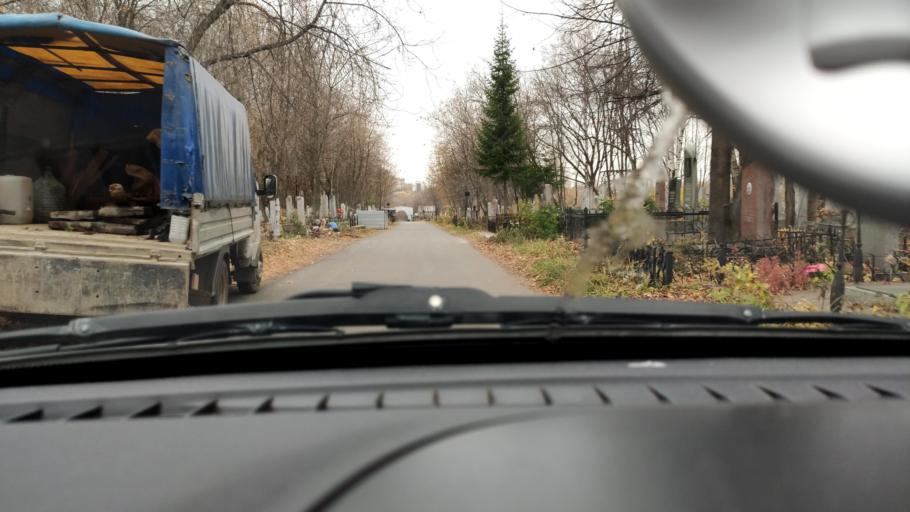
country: RU
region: Perm
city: Perm
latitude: 57.9921
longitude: 56.2826
